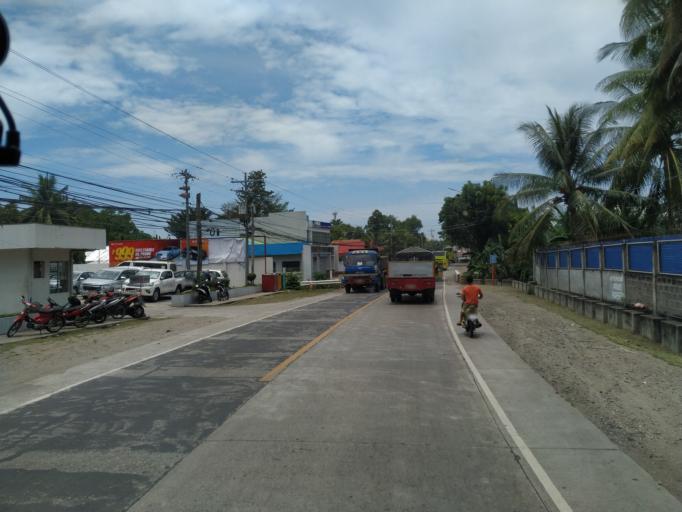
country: PH
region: Central Visayas
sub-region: Province of Negros Oriental
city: Sibulan
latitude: 9.3544
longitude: 123.2845
